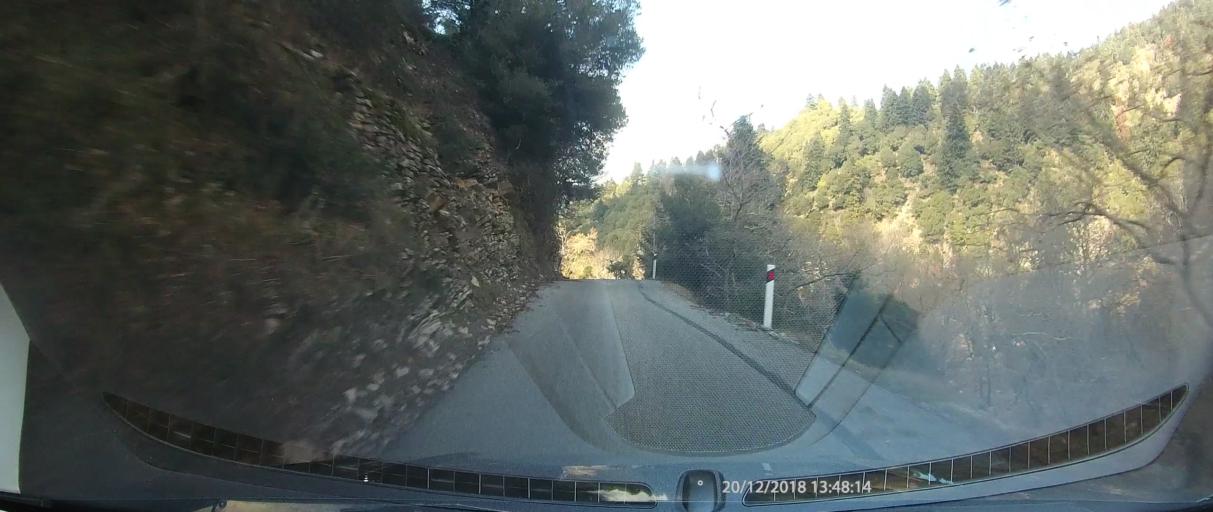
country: GR
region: West Greece
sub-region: Nomos Aitolias kai Akarnanias
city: Paravola
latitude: 38.6860
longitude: 21.6116
